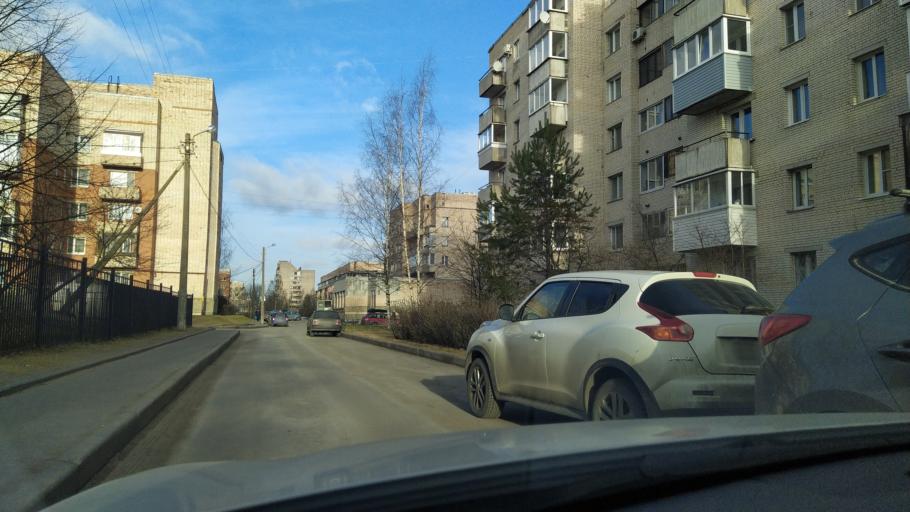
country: RU
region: St.-Petersburg
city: Pushkin
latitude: 59.7364
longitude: 30.4013
